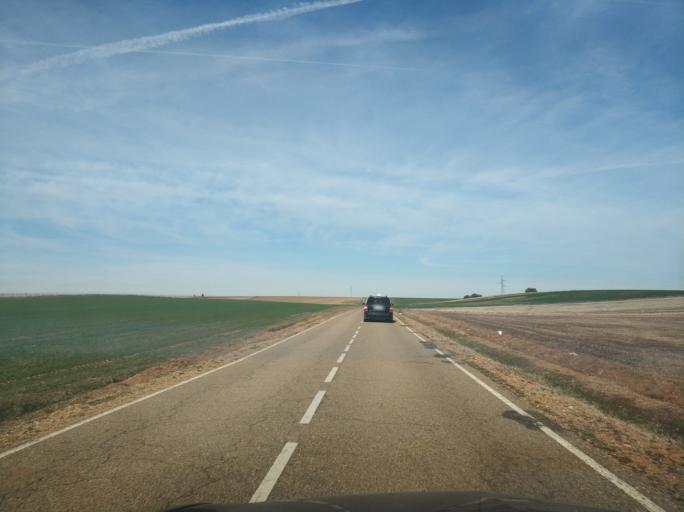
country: ES
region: Castille and Leon
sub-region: Provincia de Salamanca
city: Parada de Arriba
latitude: 40.9911
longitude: -5.8035
